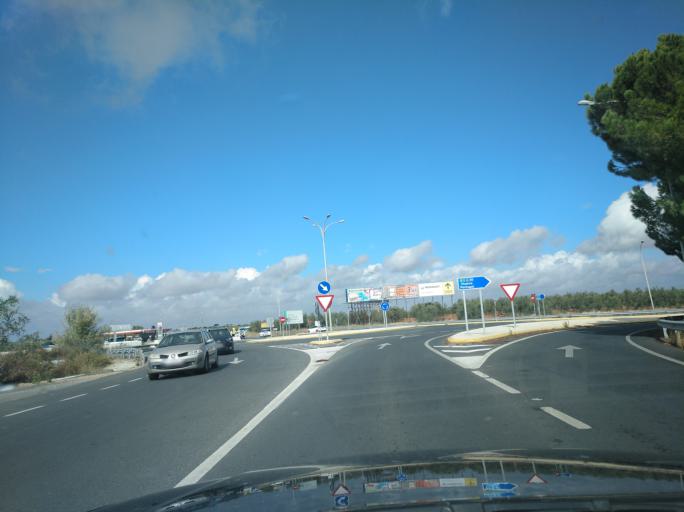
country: ES
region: Andalusia
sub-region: Provincia de Sevilla
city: Umbrete
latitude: 37.3607
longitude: -6.1420
